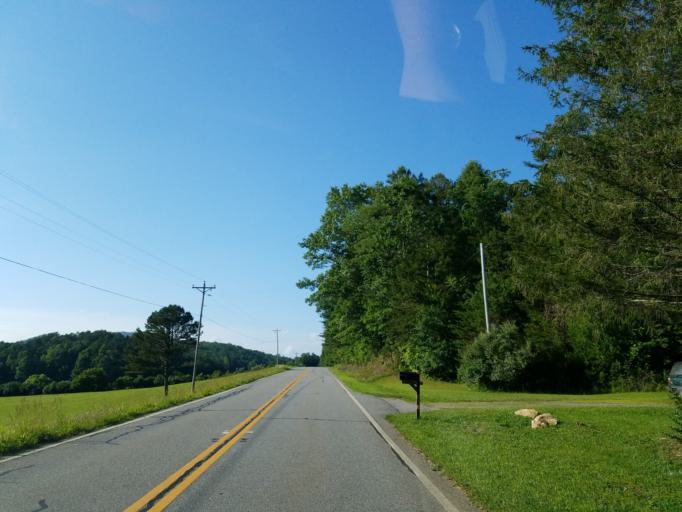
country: US
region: Georgia
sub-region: Fannin County
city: Blue Ridge
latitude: 34.7749
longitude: -84.1856
